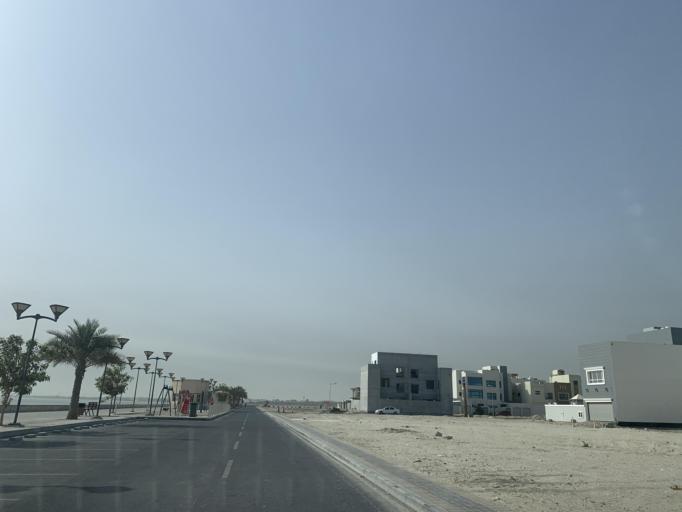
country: BH
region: Northern
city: Madinat `Isa
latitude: 26.1893
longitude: 50.5667
